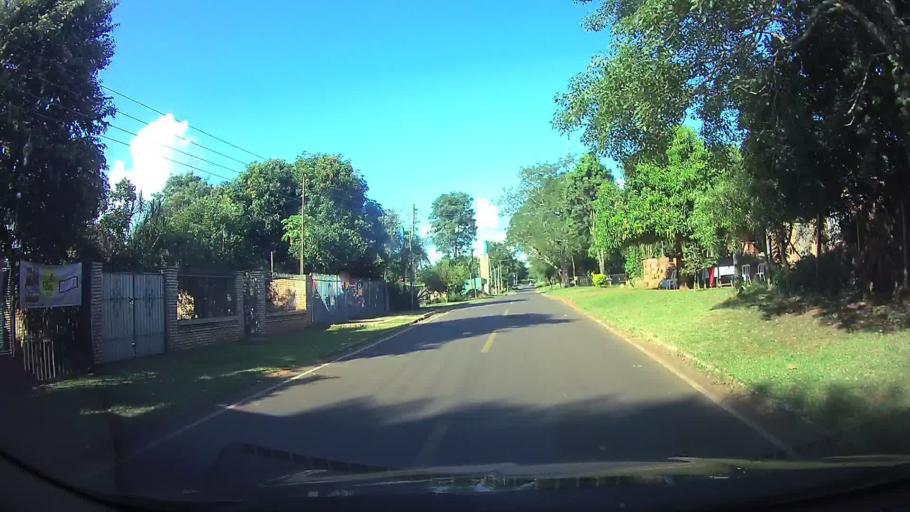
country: PY
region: Central
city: Aregua
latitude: -25.3508
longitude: -57.3934
